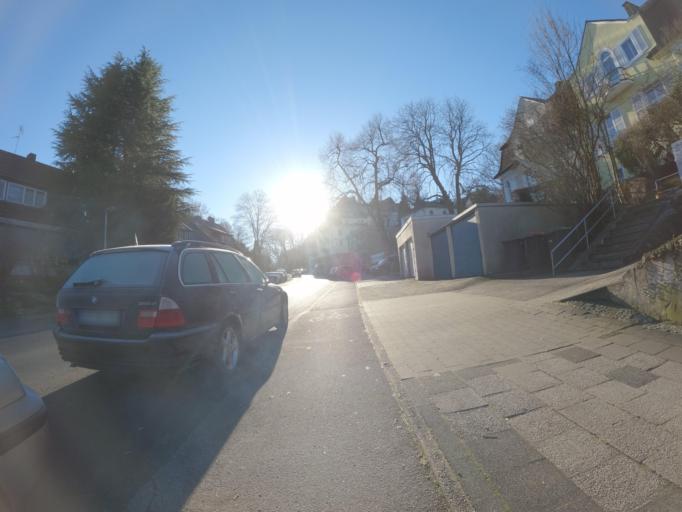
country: DE
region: North Rhine-Westphalia
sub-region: Regierungsbezirk Koln
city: Aachen
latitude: 50.7860
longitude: 6.0900
